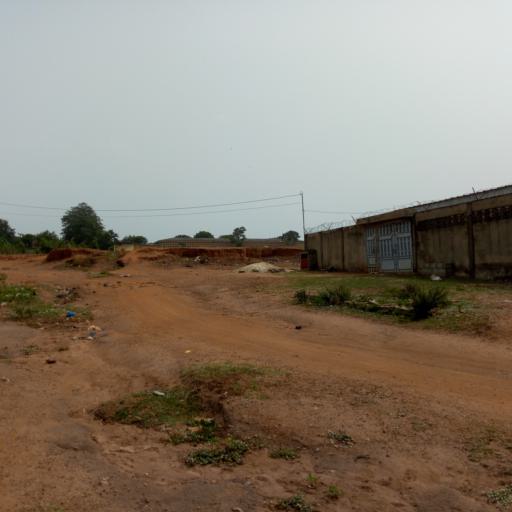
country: CI
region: Vallee du Bandama
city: Bouake
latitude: 7.7047
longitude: -5.0331
